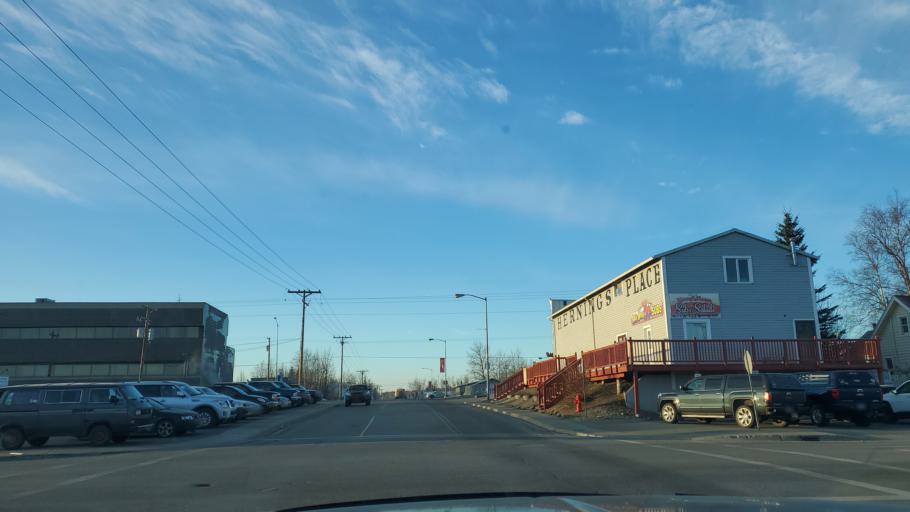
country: US
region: Alaska
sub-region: Matanuska-Susitna Borough
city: Wasilla
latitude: 61.5823
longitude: -149.4391
